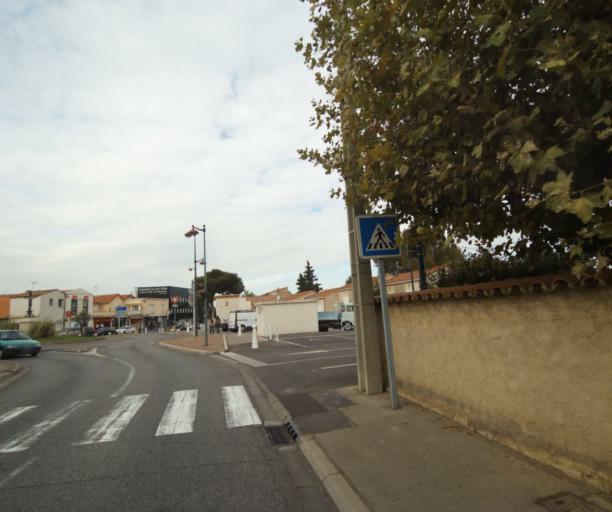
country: FR
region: Provence-Alpes-Cote d'Azur
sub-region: Departement des Bouches-du-Rhone
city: Saint-Victoret
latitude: 43.4196
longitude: 5.2381
